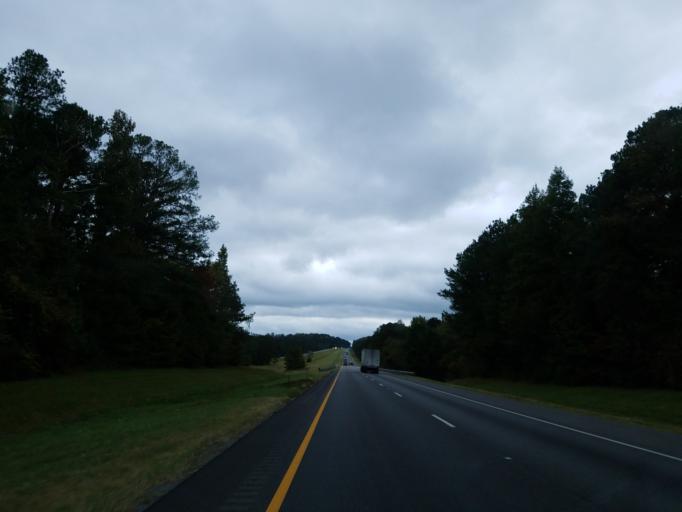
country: US
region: Alabama
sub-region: Hale County
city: Moundville
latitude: 33.0006
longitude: -87.7705
